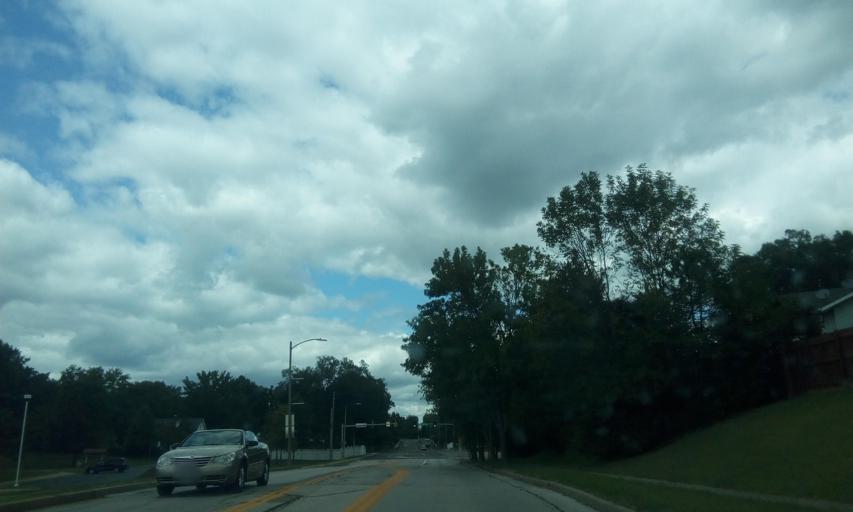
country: US
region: Missouri
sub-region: Saint Louis County
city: Ballwin
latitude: 38.6084
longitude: -90.5385
